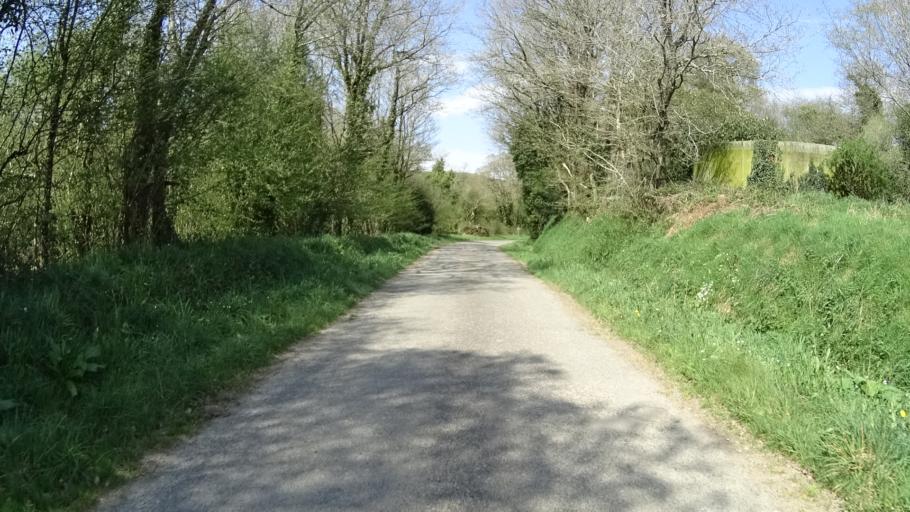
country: FR
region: Brittany
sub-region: Departement du Finistere
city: Sizun
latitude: 48.4349
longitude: -4.1019
